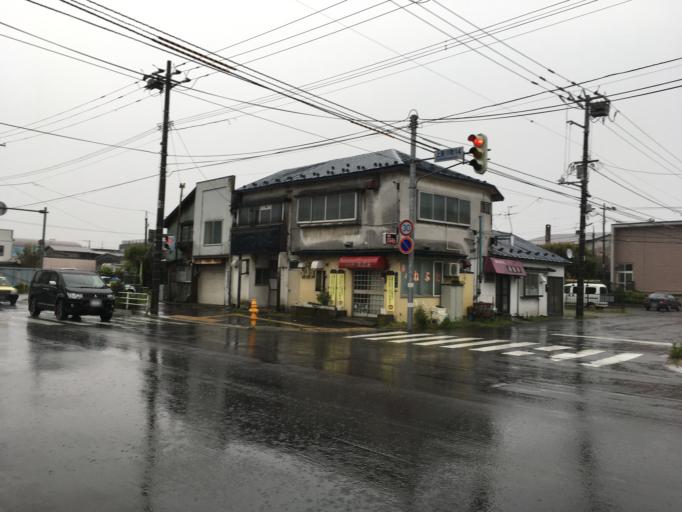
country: JP
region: Hokkaido
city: Hakodate
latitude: 41.7811
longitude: 140.7370
